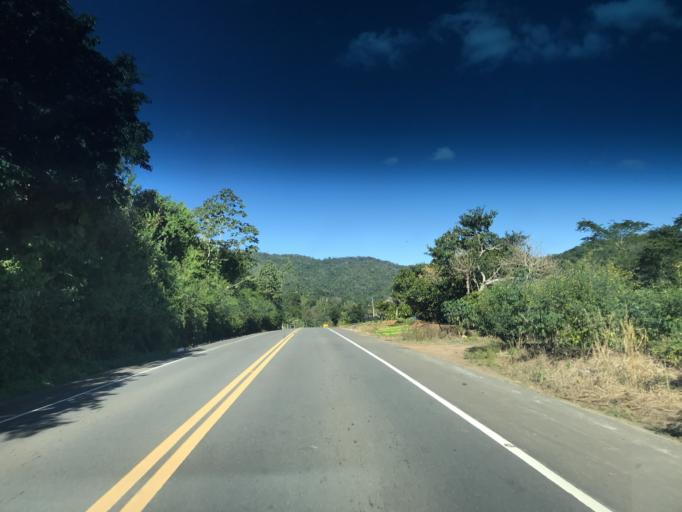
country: BR
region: Bahia
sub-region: Gandu
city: Gandu
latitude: -13.8858
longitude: -39.4832
